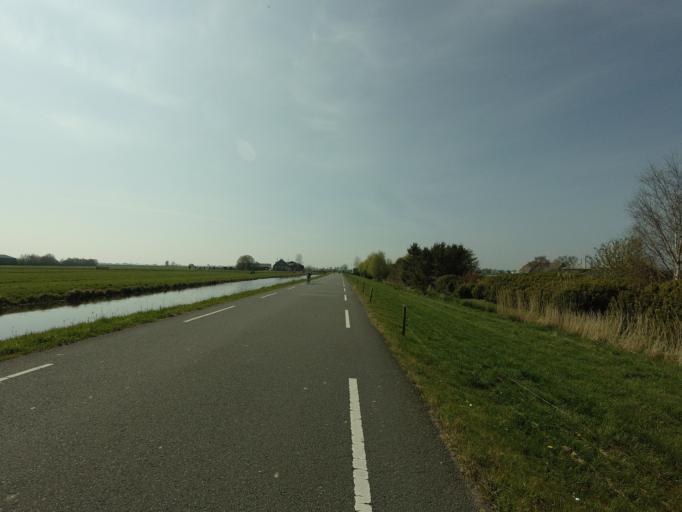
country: NL
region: South Holland
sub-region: Gemeente Nieuwkoop
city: Nieuwkoop
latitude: 52.1344
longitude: 4.7179
